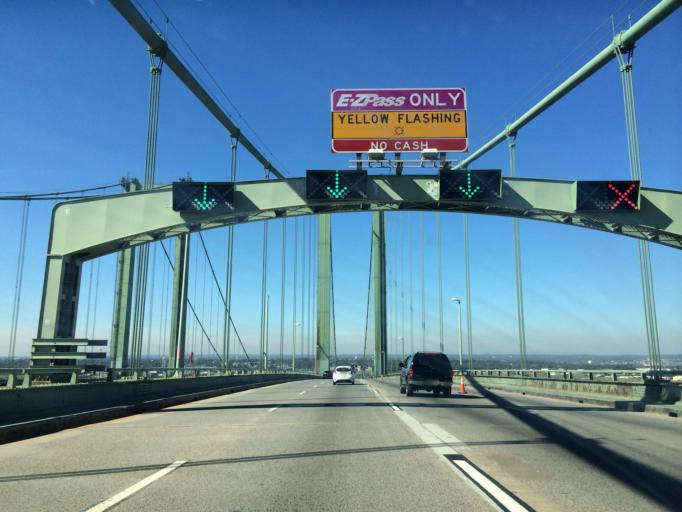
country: US
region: New Jersey
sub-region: Salem County
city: Pennsville
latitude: 39.6894
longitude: -75.5189
